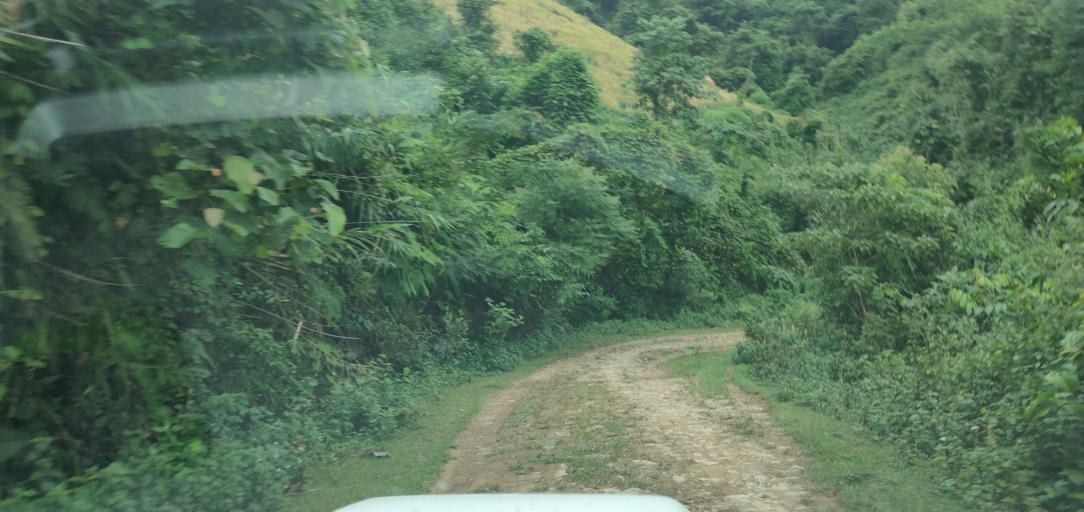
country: LA
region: Phongsali
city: Phongsali
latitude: 21.4415
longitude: 102.3209
